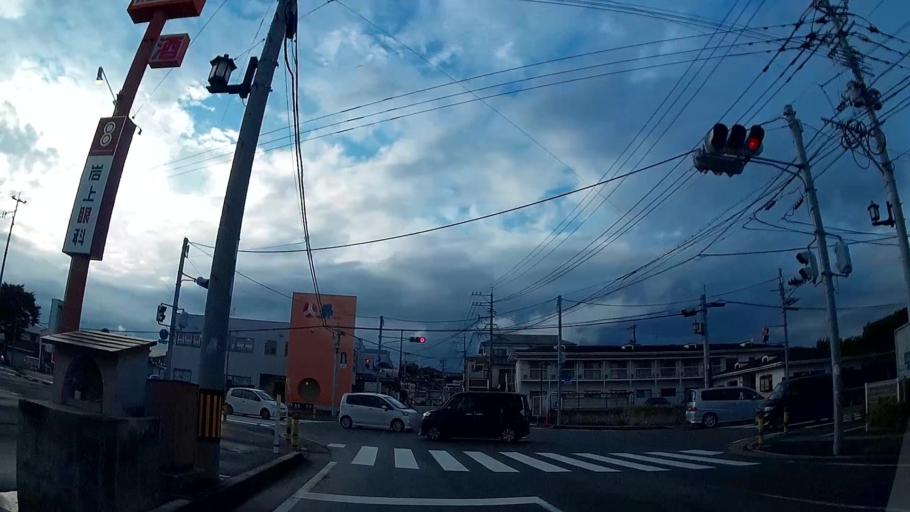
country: JP
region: Kumamoto
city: Ozu
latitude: 32.8761
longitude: 130.8702
